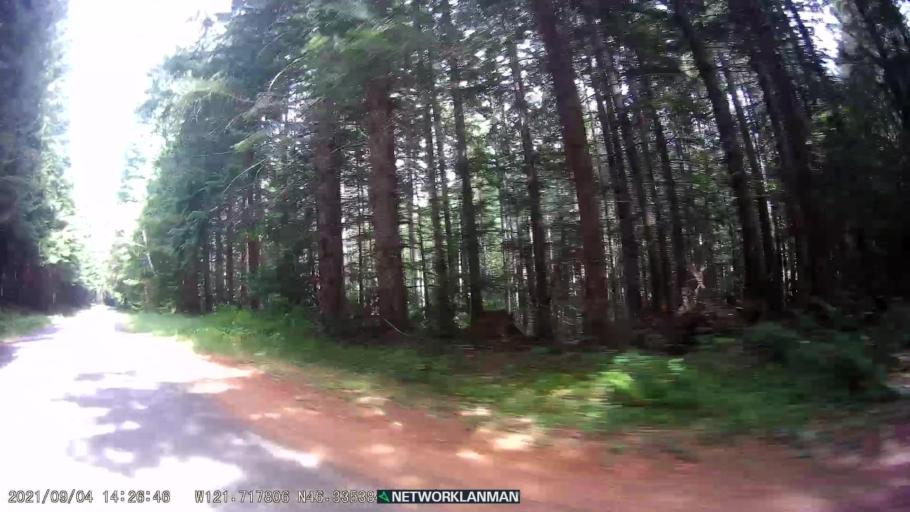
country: US
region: Washington
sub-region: Lewis County
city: Morton
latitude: 46.3352
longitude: -121.7169
